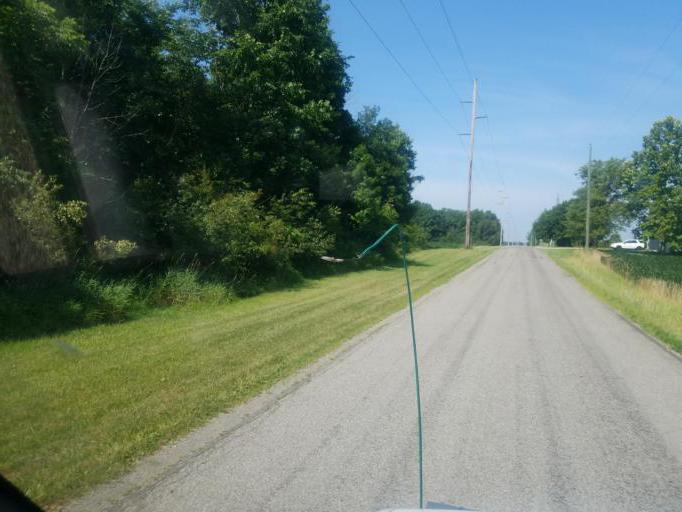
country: US
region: Ohio
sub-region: Union County
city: Marysville
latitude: 40.2879
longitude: -83.3667
